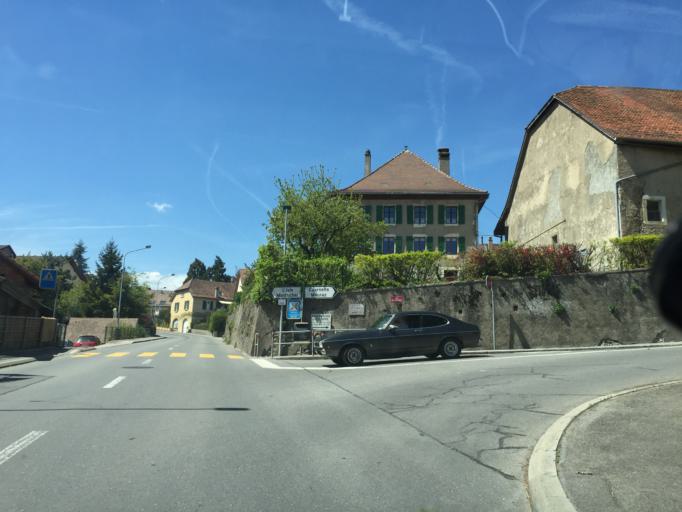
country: CH
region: Vaud
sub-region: Morges District
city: Pampigny
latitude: 46.5798
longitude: 6.4306
